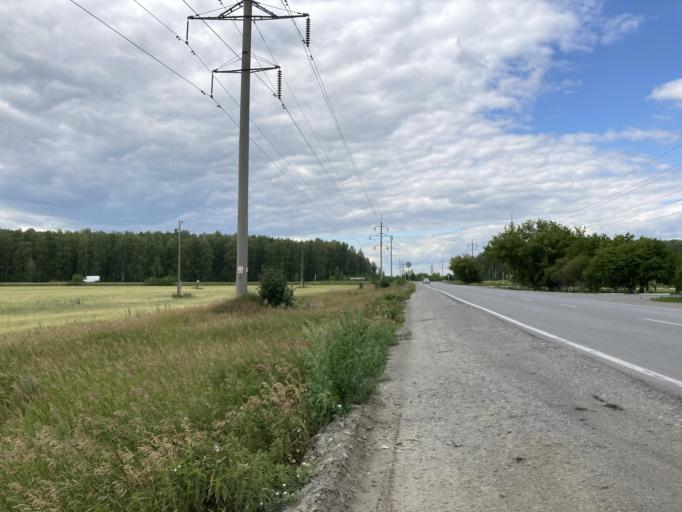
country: RU
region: Sverdlovsk
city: Bogdanovich
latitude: 56.8056
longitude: 62.0347
